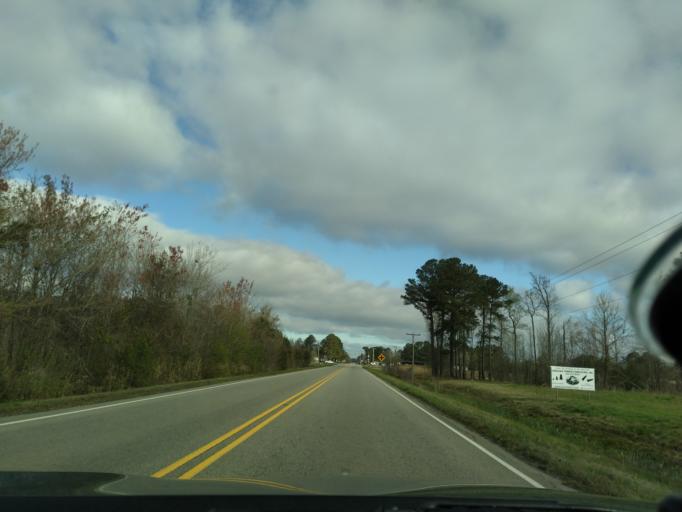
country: US
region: North Carolina
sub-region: Washington County
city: Plymouth
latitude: 35.8893
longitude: -76.7008
